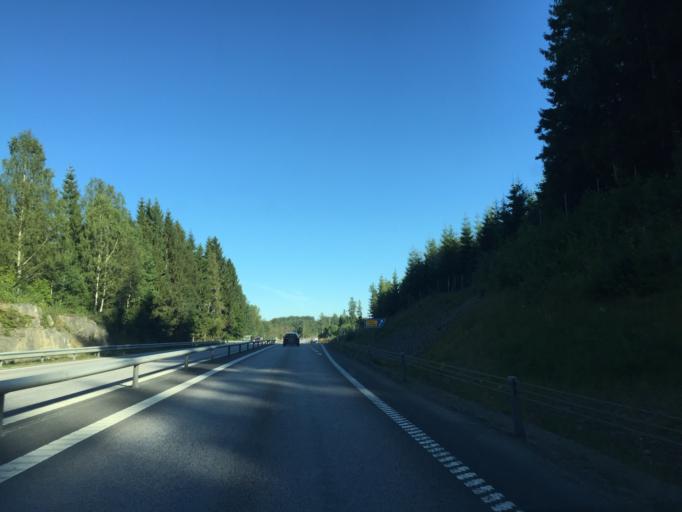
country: SE
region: OErebro
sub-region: Lekebergs Kommun
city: Fjugesta
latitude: 59.2672
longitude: 14.7921
